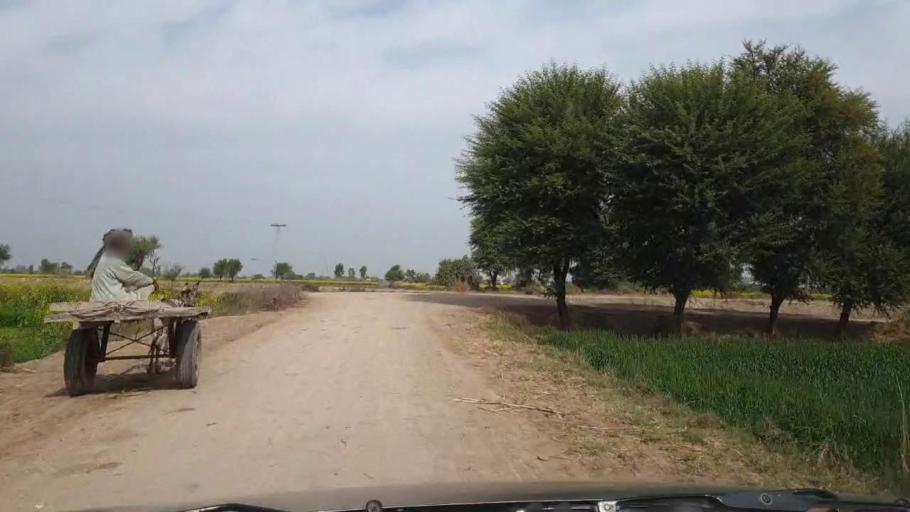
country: PK
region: Sindh
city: Sanghar
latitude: 26.0987
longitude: 68.8814
